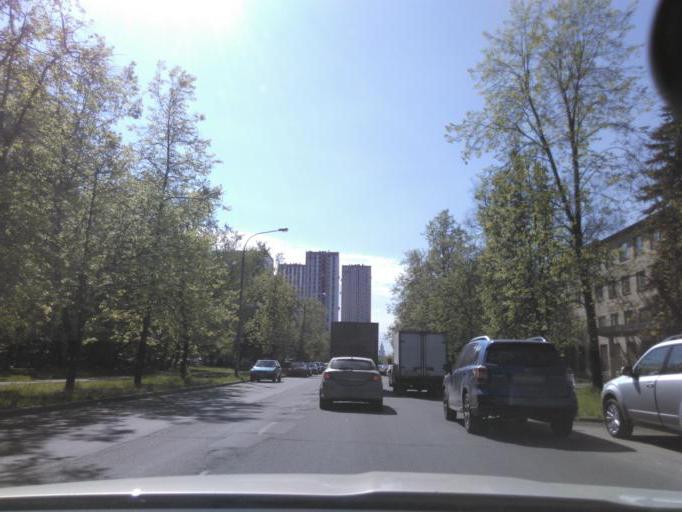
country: RU
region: Moskovskaya
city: Levoberezhnyy
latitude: 55.8448
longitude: 37.4904
